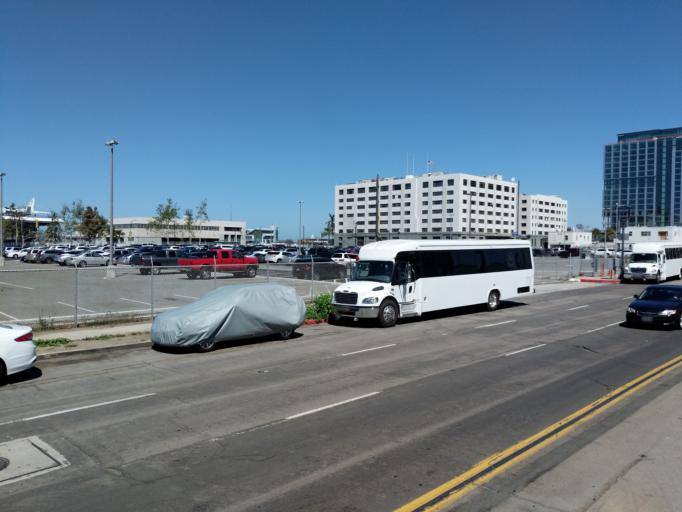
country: US
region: California
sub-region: San Diego County
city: San Diego
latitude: 32.7132
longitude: -117.1710
